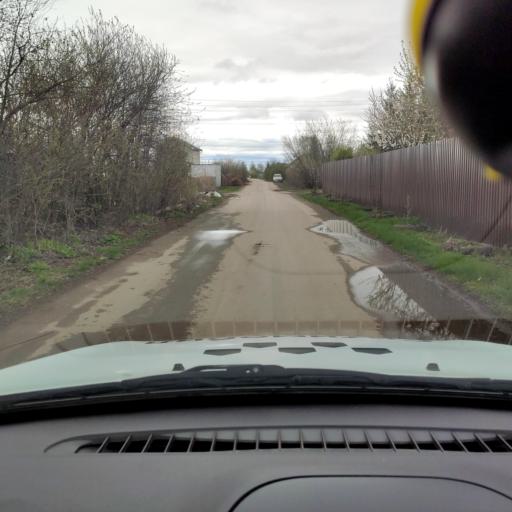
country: RU
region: Samara
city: Tol'yatti
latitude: 53.5813
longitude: 49.3213
